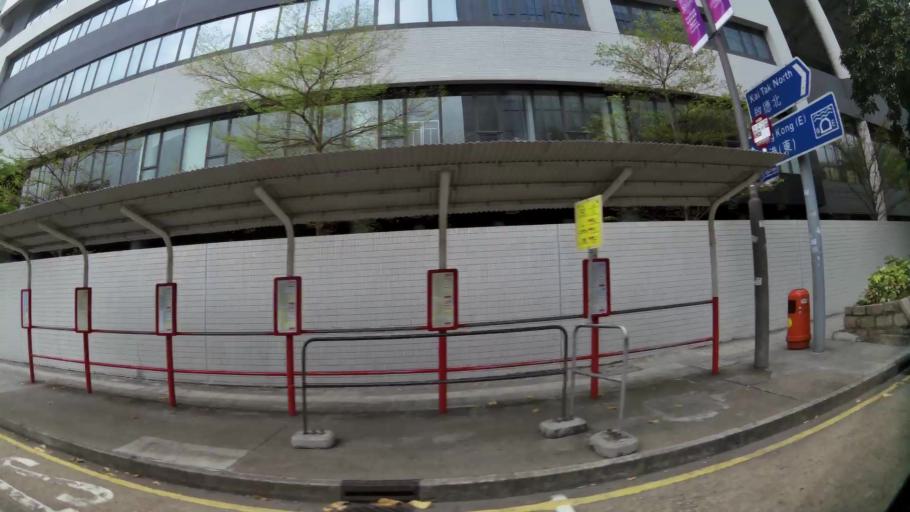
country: HK
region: Kowloon City
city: Kowloon
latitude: 22.3256
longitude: 114.2070
